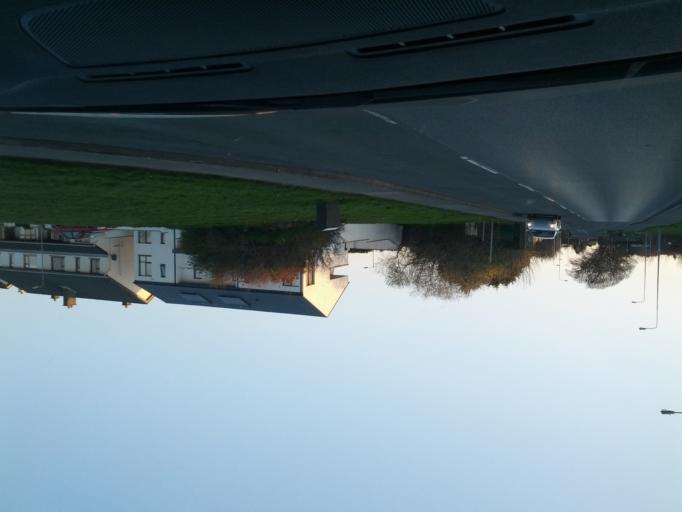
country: IE
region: Connaught
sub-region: County Galway
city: Gaillimh
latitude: 53.2760
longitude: -9.0828
